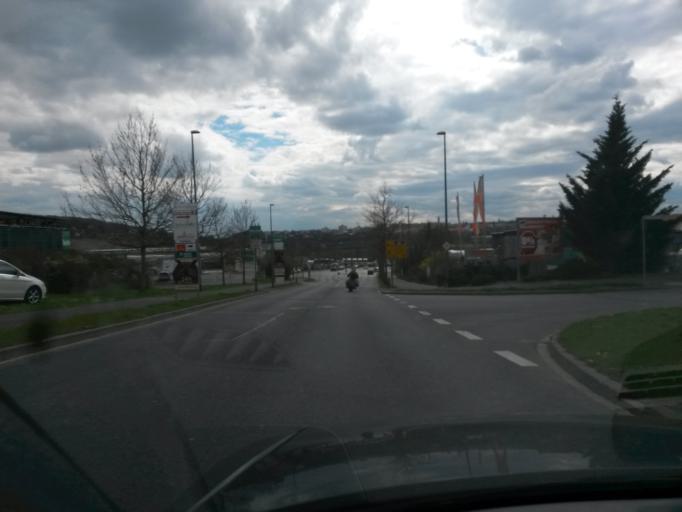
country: DE
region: Bavaria
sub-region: Regierungsbezirk Unterfranken
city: Gerbrunn
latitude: 49.7936
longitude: 10.0021
